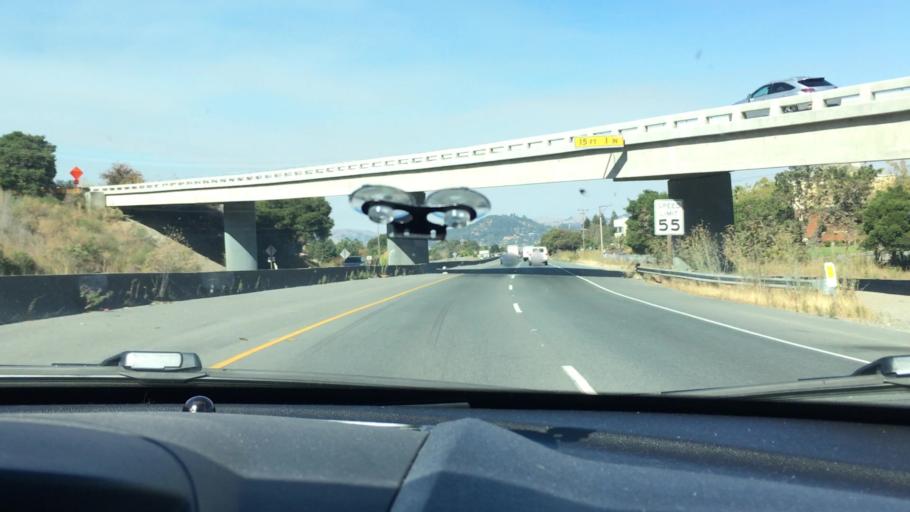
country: US
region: California
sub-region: Marin County
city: Corte Madera
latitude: 37.9461
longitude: -122.4907
